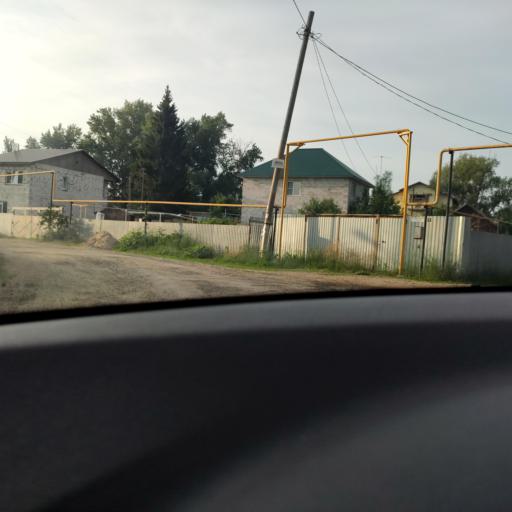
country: RU
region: Samara
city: Rozhdestveno
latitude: 53.1505
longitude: 50.0247
